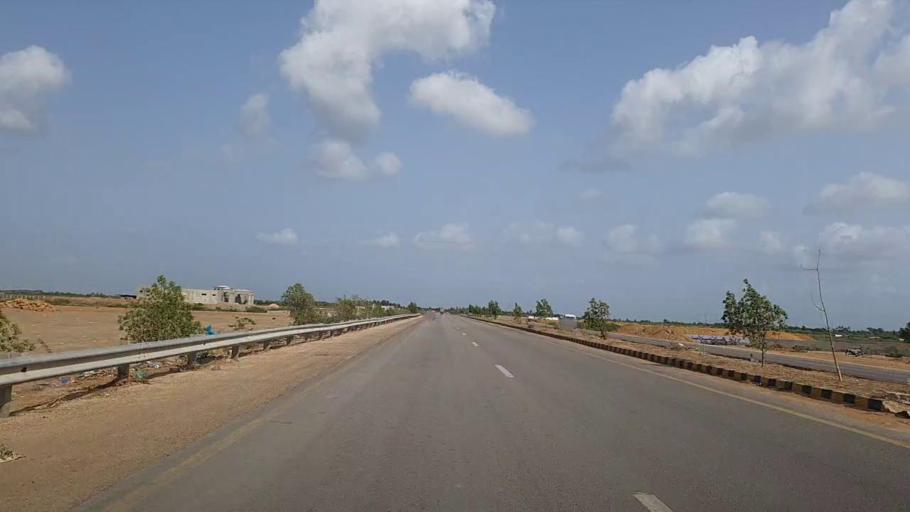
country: PK
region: Sindh
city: Gharo
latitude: 24.7355
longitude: 67.6000
